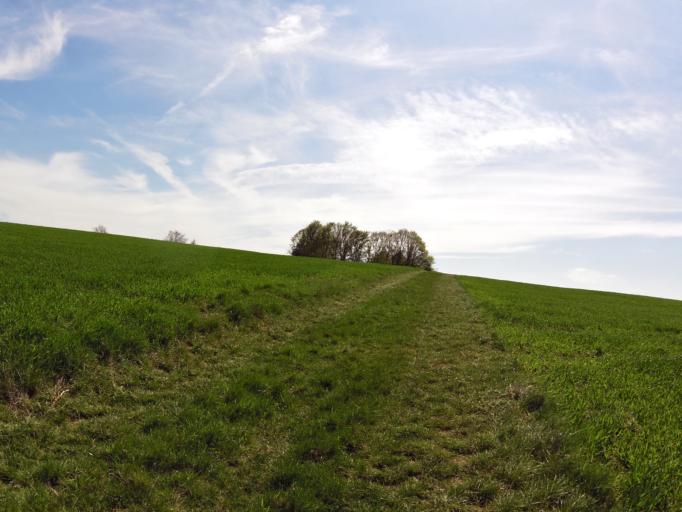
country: DE
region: Bavaria
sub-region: Regierungsbezirk Unterfranken
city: Rottendorf
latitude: 49.7953
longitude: 10.0463
